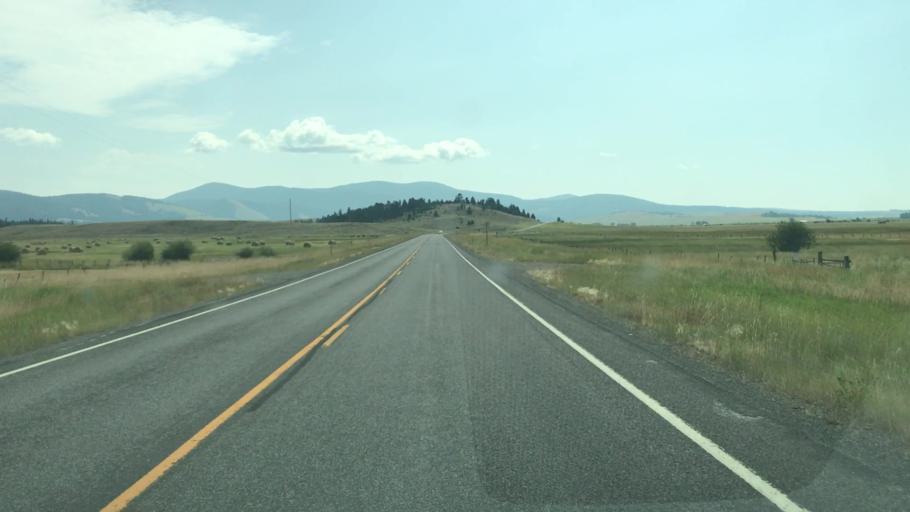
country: US
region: Montana
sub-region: Lewis and Clark County
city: Lincoln
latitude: 46.7748
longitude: -112.7433
